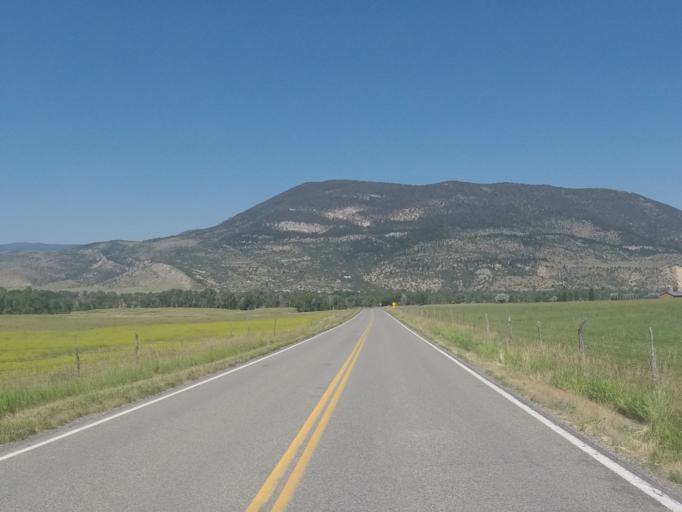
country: US
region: Montana
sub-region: Park County
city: Livingston
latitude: 45.5702
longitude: -110.5623
